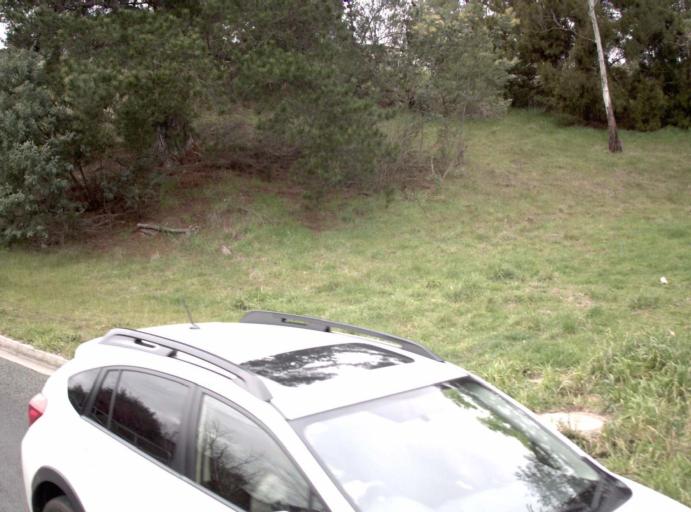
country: AU
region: Tasmania
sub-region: Launceston
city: Newstead
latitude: -41.4501
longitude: 147.1749
